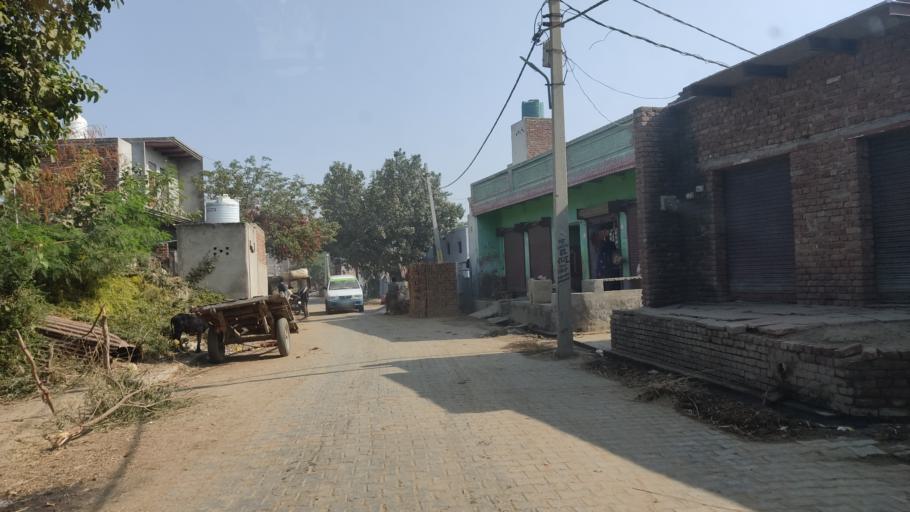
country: IN
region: Uttar Pradesh
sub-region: Mathura
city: Radha Kund
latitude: 27.5561
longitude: 77.5577
